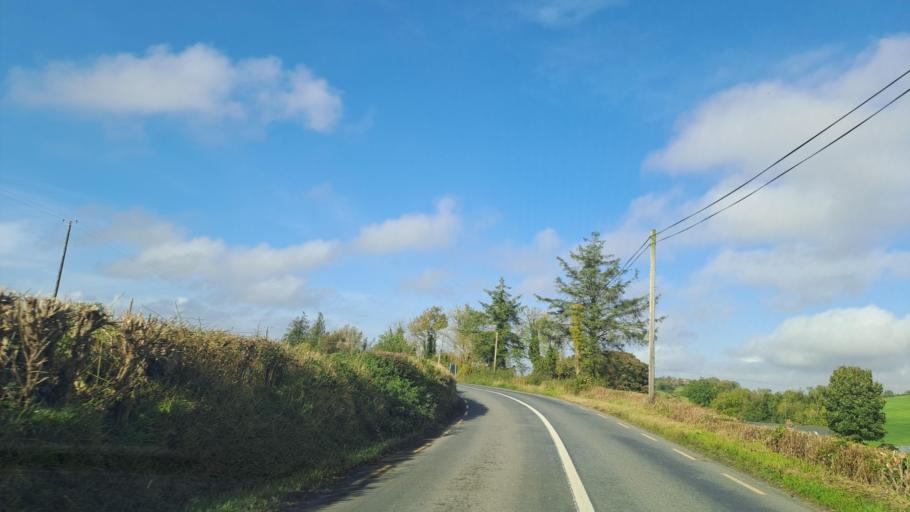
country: IE
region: Ulster
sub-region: An Cabhan
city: Cootehill
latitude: 54.0659
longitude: -7.0517
